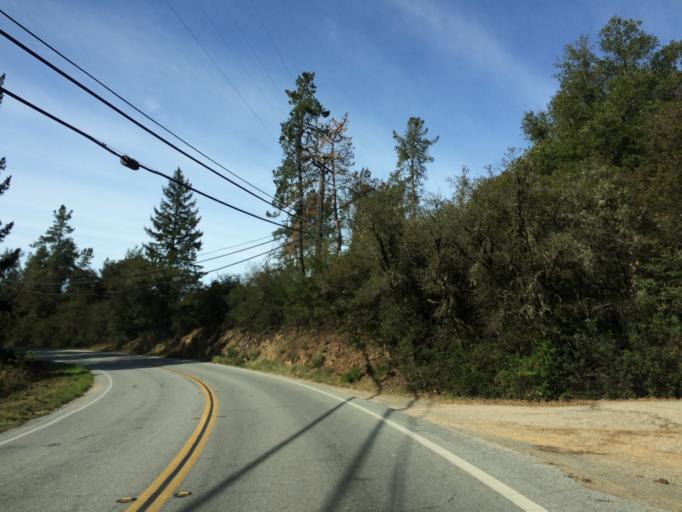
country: US
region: California
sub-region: Santa Cruz County
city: Bonny Doon
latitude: 37.0599
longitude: -122.1238
